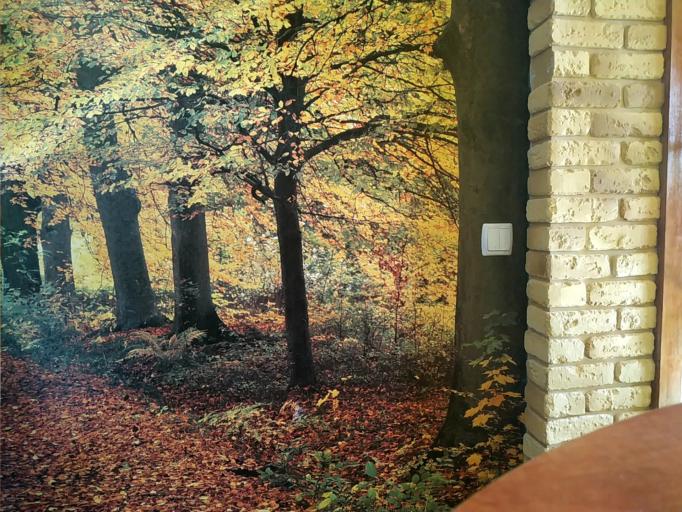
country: RU
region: Jaroslavl
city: Kukoboy
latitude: 58.8321
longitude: 39.7541
